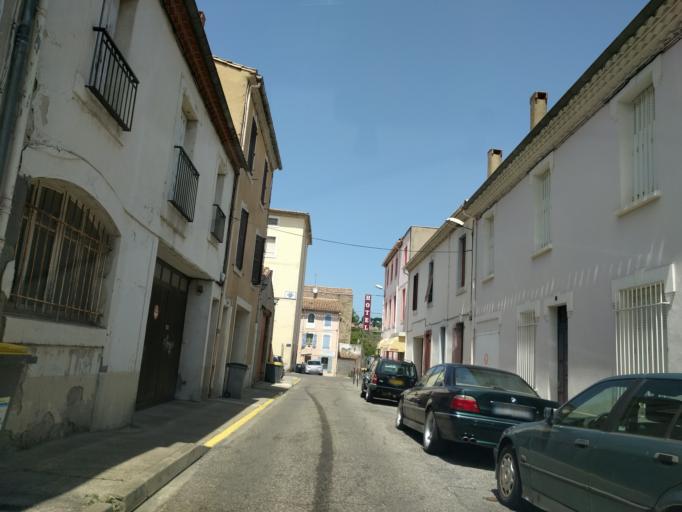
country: FR
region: Languedoc-Roussillon
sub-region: Departement de l'Aude
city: Carcassonne
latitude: 43.2172
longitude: 2.3541
